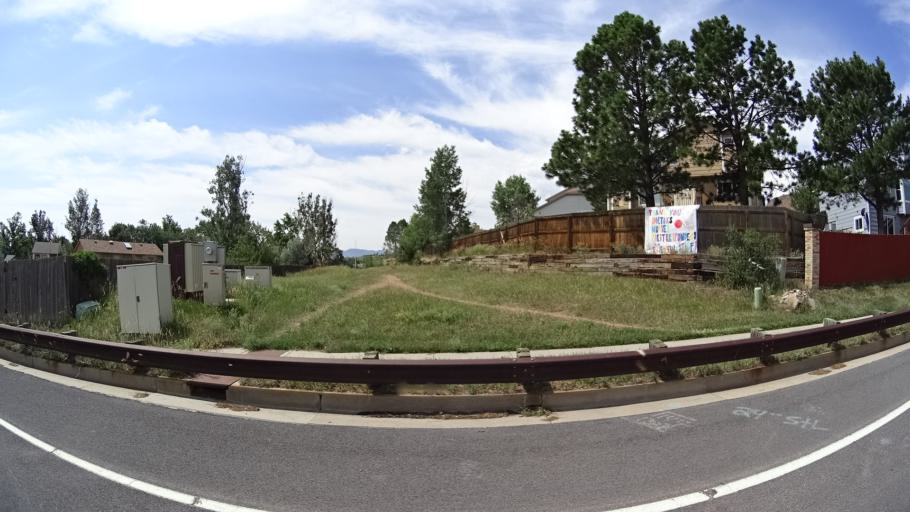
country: US
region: Colorado
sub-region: El Paso County
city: Air Force Academy
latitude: 38.9367
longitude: -104.8747
